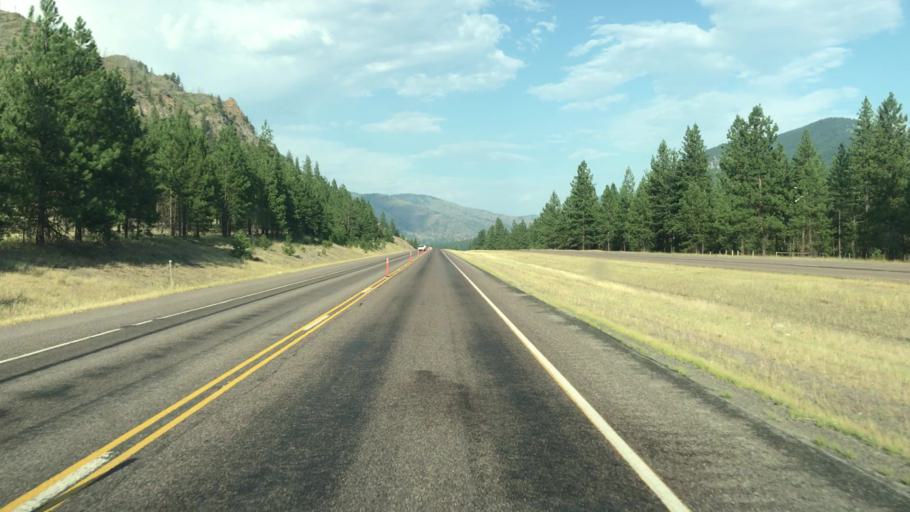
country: US
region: Montana
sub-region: Mineral County
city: Superior
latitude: 47.0119
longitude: -114.7155
